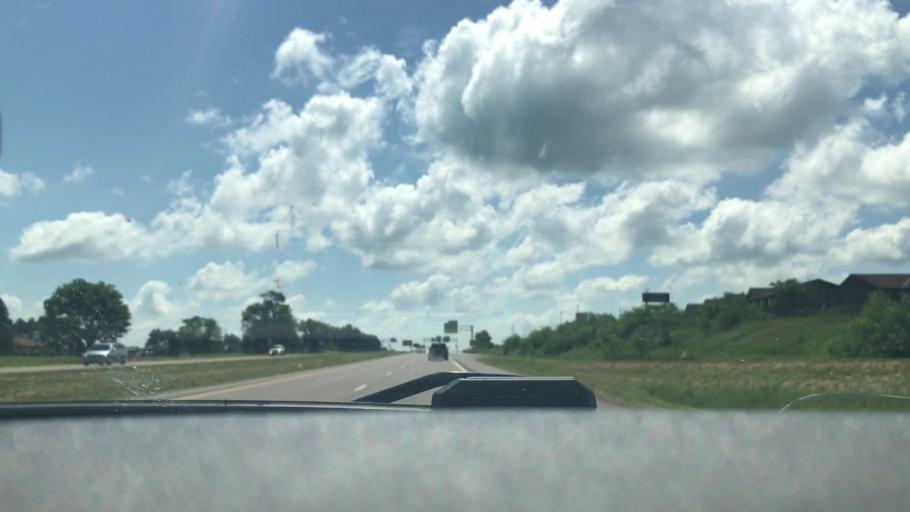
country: US
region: Wisconsin
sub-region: Eau Claire County
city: Altoona
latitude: 44.7767
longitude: -91.4346
